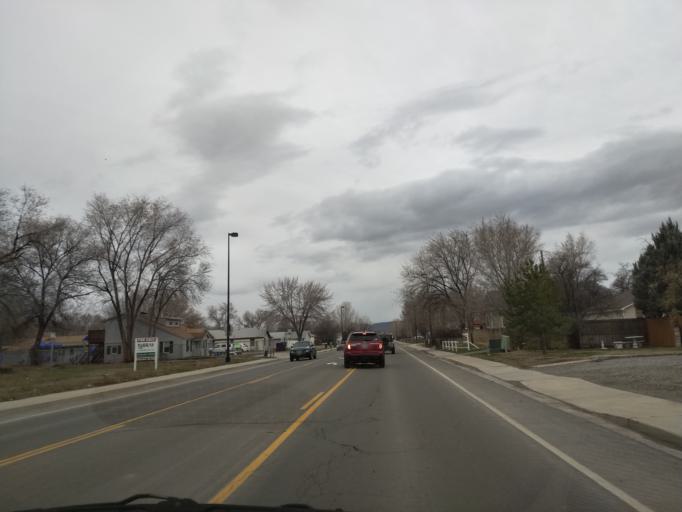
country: US
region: Colorado
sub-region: Mesa County
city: Fruitvale
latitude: 39.0815
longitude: -108.5152
